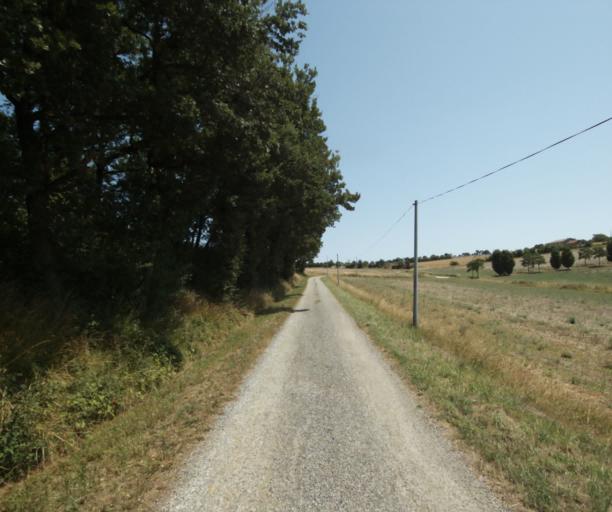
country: FR
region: Midi-Pyrenees
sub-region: Departement de la Haute-Garonne
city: Saint-Felix-Lauragais
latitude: 43.4542
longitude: 1.8495
